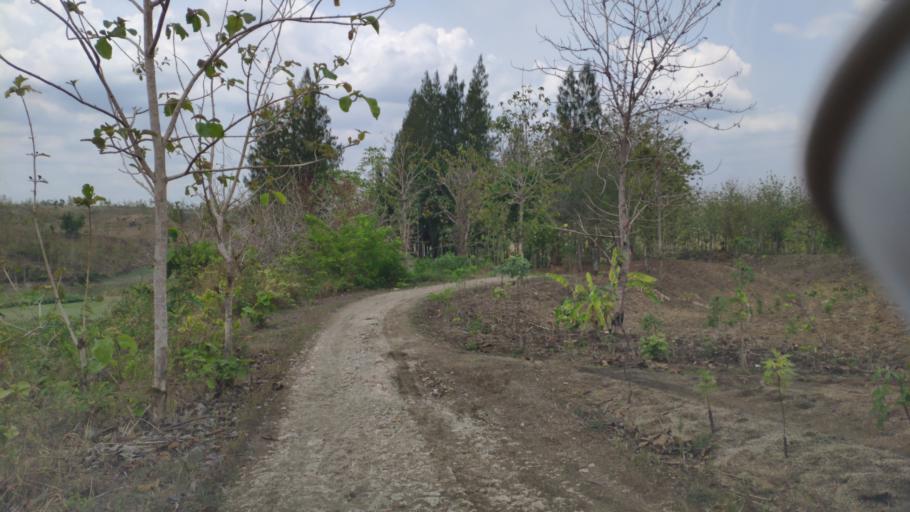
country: ID
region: Central Java
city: Gumiring
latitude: -7.0501
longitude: 111.3975
